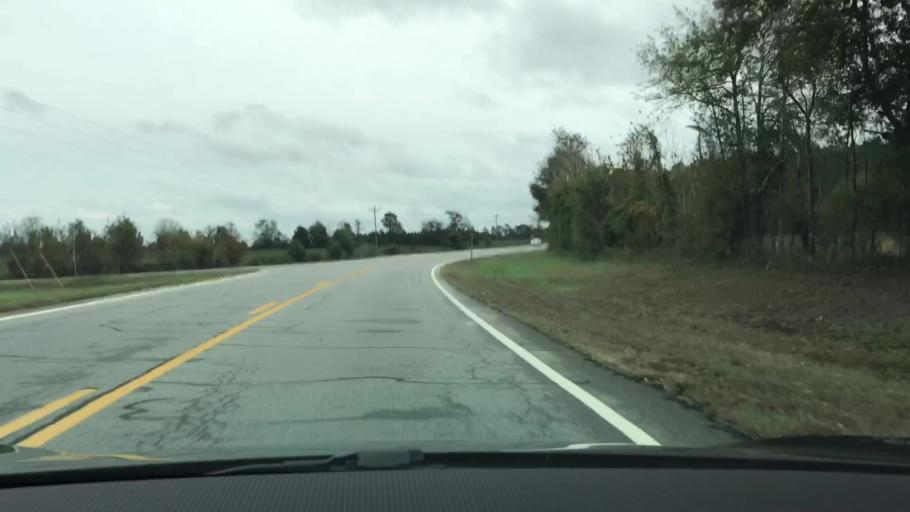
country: US
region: Georgia
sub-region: Glascock County
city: Gibson
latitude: 33.3315
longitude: -82.5626
